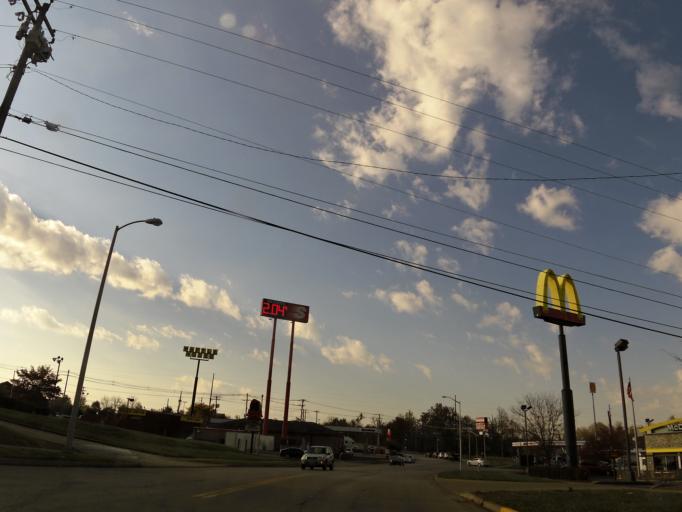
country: US
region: Kentucky
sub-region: Fayette County
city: Lexington-Fayette
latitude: 38.0428
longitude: -84.4233
